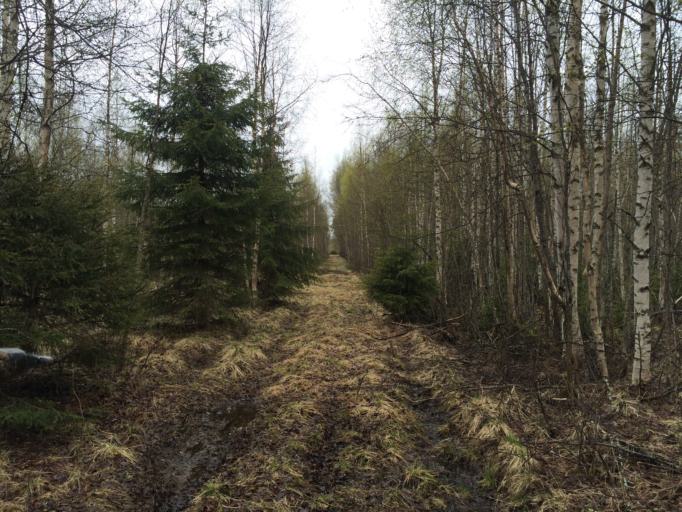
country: SE
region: Norrbotten
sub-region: Bodens Kommun
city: Saevast
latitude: 65.7126
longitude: 21.8325
